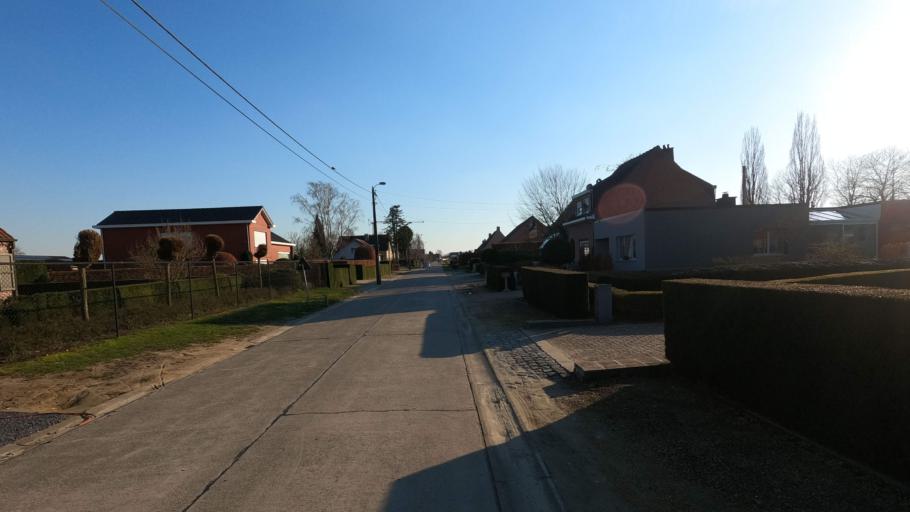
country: BE
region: Flanders
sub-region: Provincie Antwerpen
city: Berlaar
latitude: 51.0910
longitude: 4.6437
